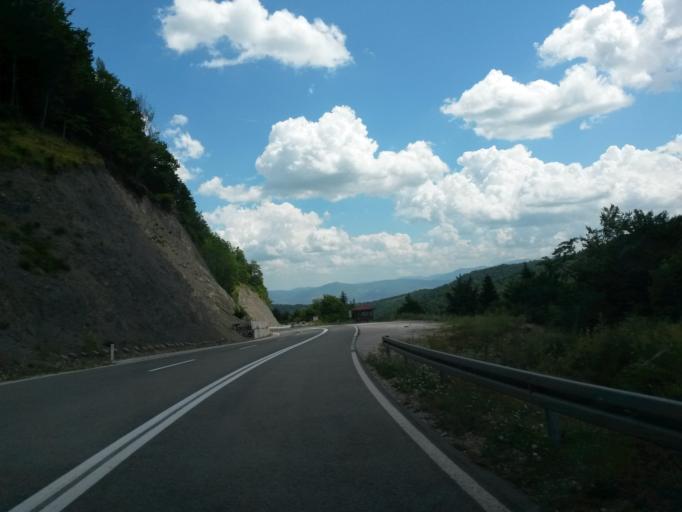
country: BA
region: Federation of Bosnia and Herzegovina
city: Bugojno
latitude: 44.0236
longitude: 17.3335
